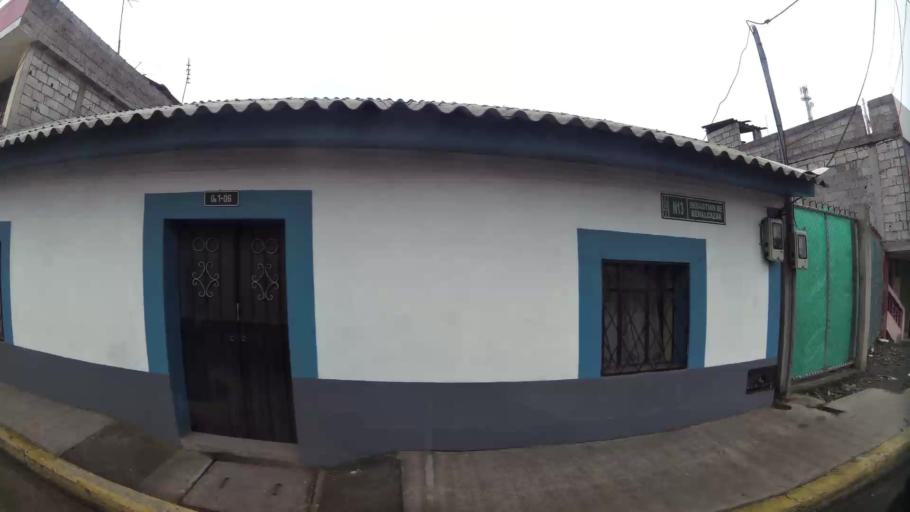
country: EC
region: Pichincha
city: Sangolqui
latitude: -0.2676
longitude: -78.4640
